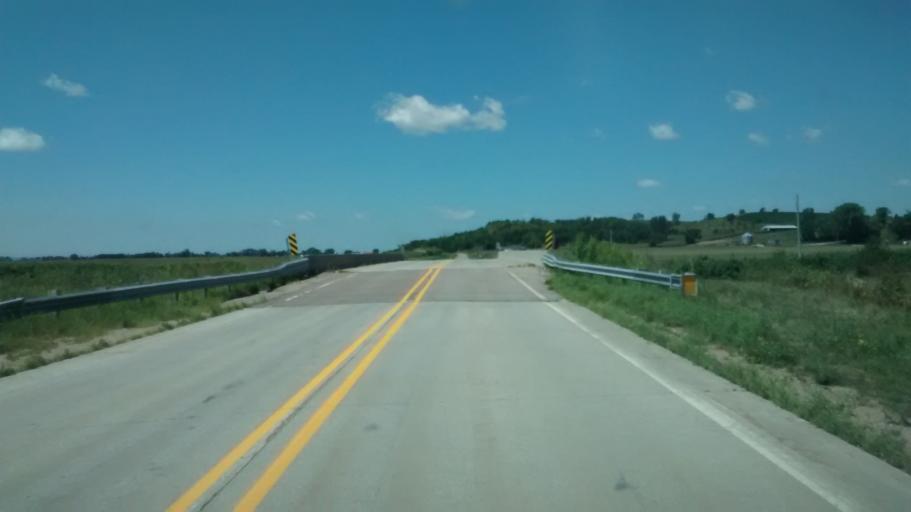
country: US
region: Iowa
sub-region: Woodbury County
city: Moville
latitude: 42.2643
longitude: -96.0528
